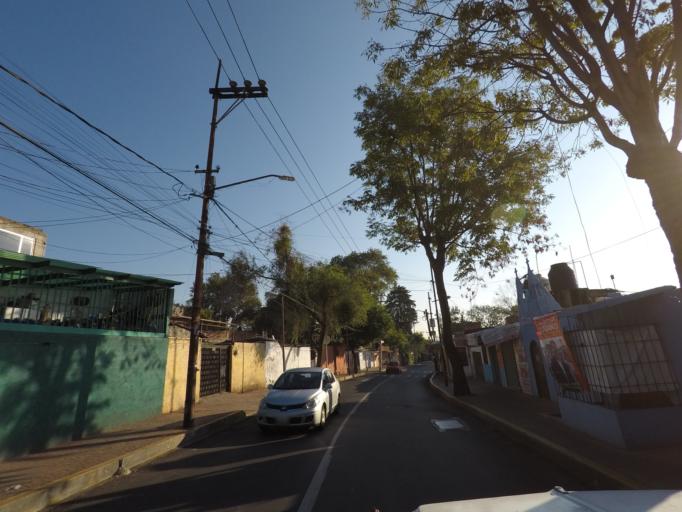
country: MX
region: Mexico City
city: Magdalena Contreras
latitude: 19.3094
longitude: -99.2463
